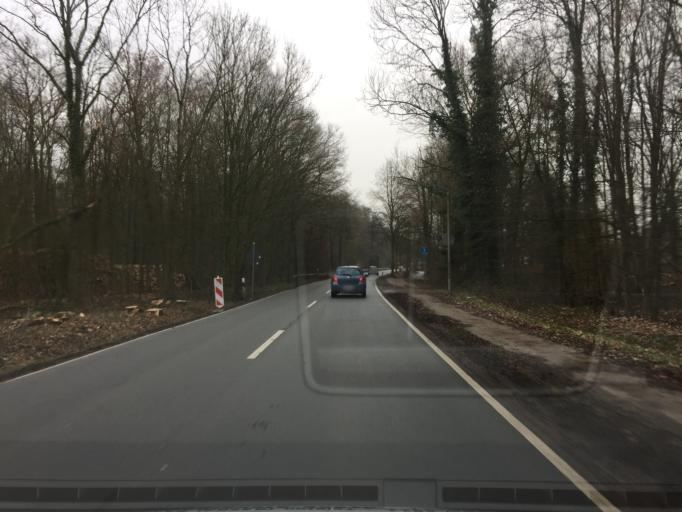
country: DE
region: Lower Saxony
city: Wiedensahl
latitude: 52.3704
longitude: 9.1299
